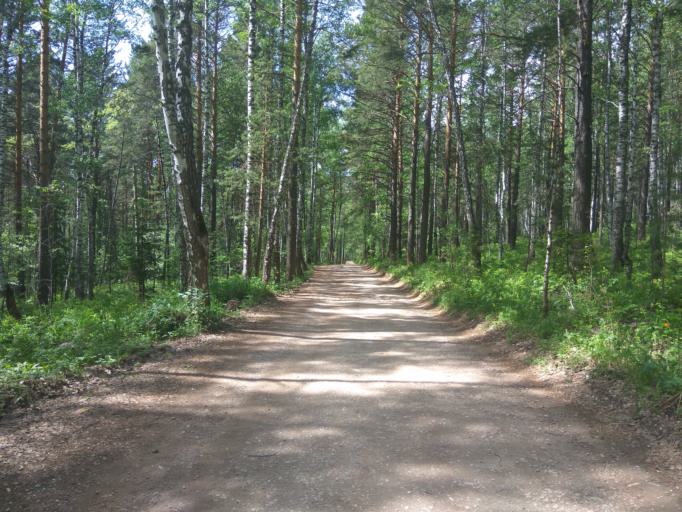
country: RU
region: Krasnoyarskiy
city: Krasnoyarsk
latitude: 55.9322
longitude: 92.9339
